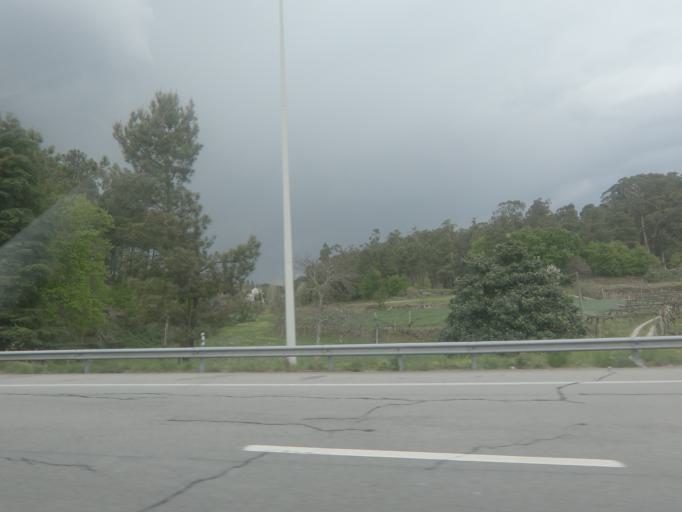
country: PT
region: Porto
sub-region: Marco de Canaveses
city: Marco de Canavezes
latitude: 41.2243
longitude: -8.1418
